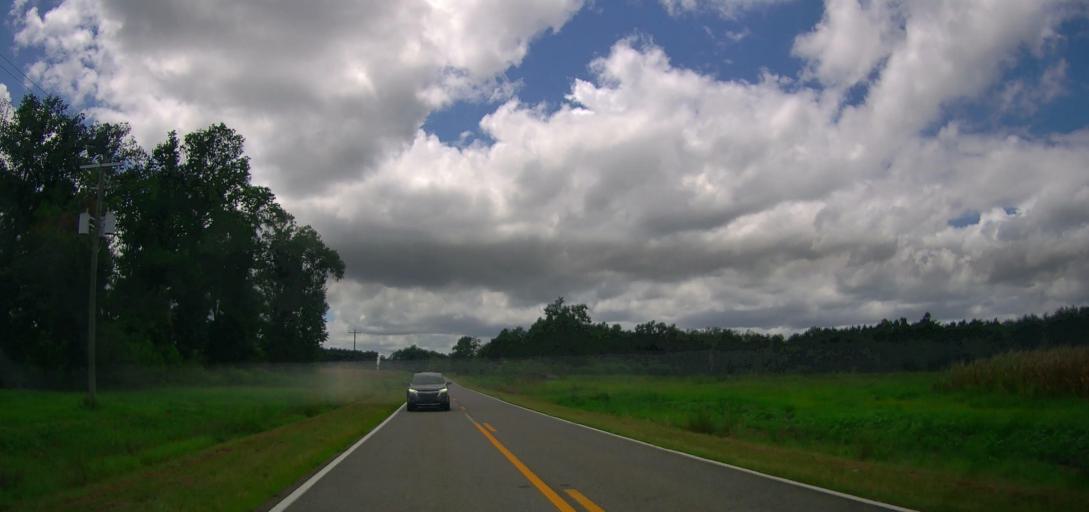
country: US
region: Georgia
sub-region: Irwin County
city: Ocilla
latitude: 31.6459
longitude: -83.3292
